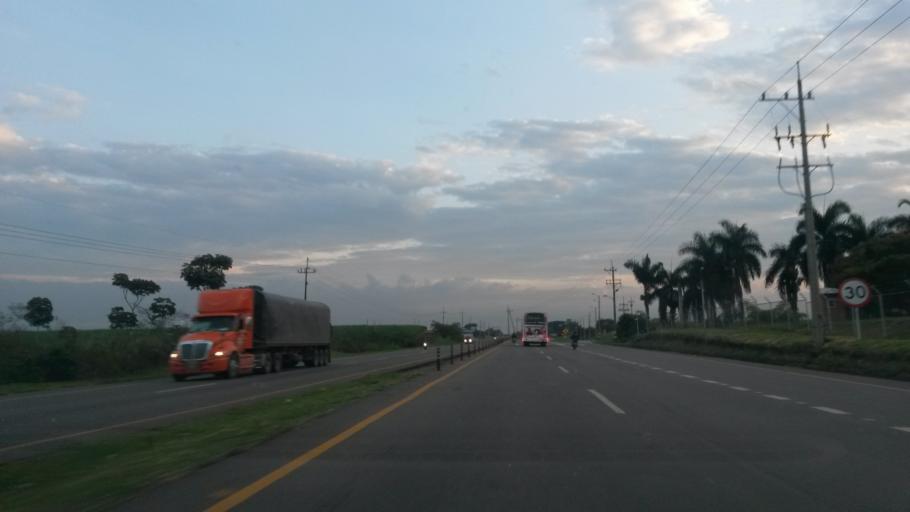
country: CO
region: Cauca
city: Caloto
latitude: 3.1276
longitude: -76.4643
